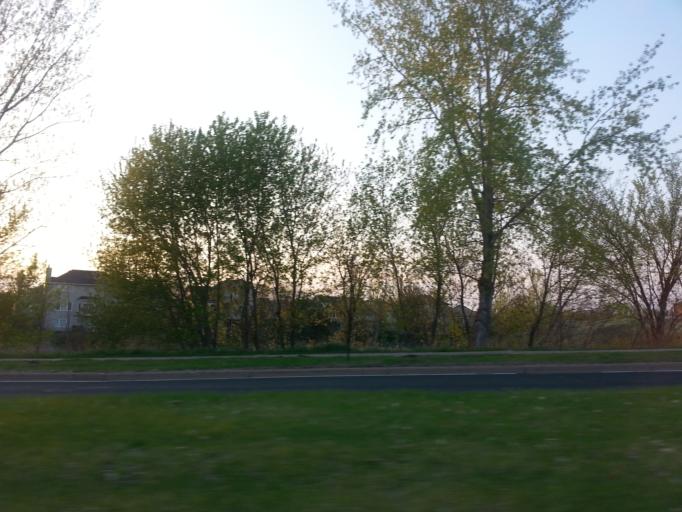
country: US
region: Minnesota
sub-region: Scott County
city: Prior Lake
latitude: 44.7397
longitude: -93.4258
